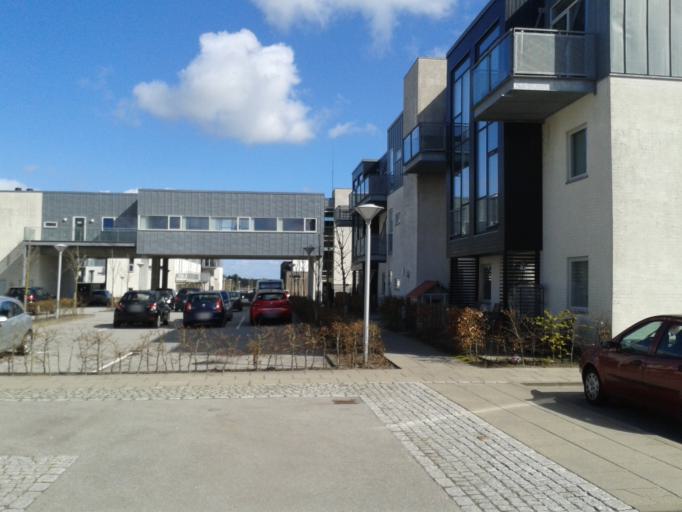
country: DK
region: North Denmark
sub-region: Alborg Kommune
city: Gistrup
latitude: 57.0116
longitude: 9.9635
